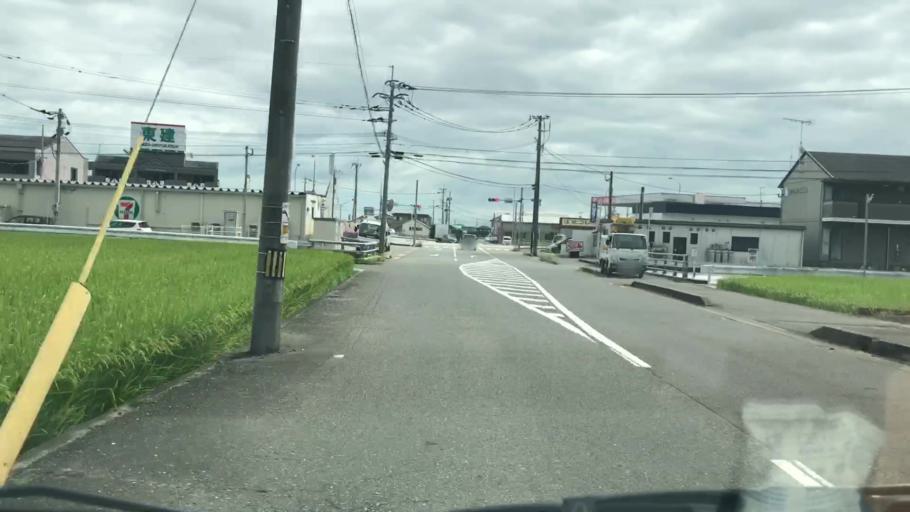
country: JP
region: Saga Prefecture
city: Saga-shi
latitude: 33.2198
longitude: 130.1693
